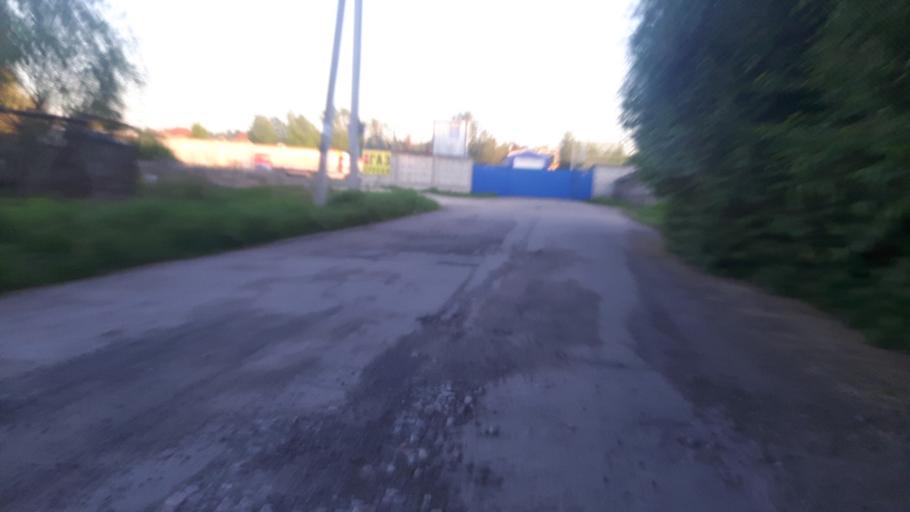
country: RU
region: St.-Petersburg
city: Bol'shaya Izhora
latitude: 59.9427
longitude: 29.5736
